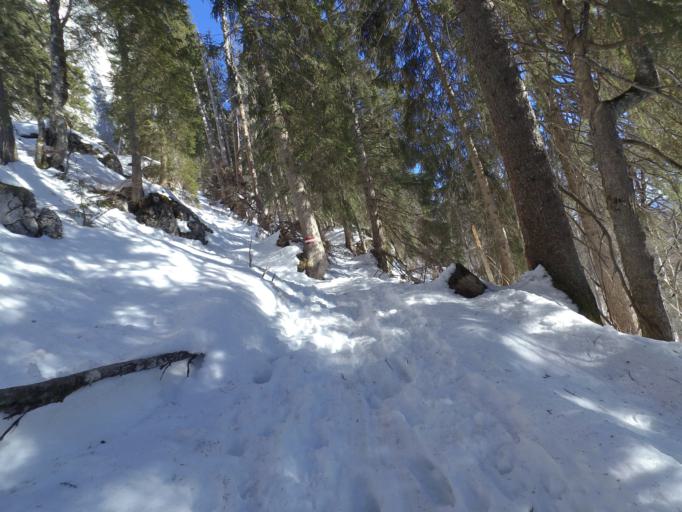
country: AT
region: Salzburg
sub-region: Politischer Bezirk Hallein
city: Scheffau am Tennengebirge
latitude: 47.6338
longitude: 13.2608
